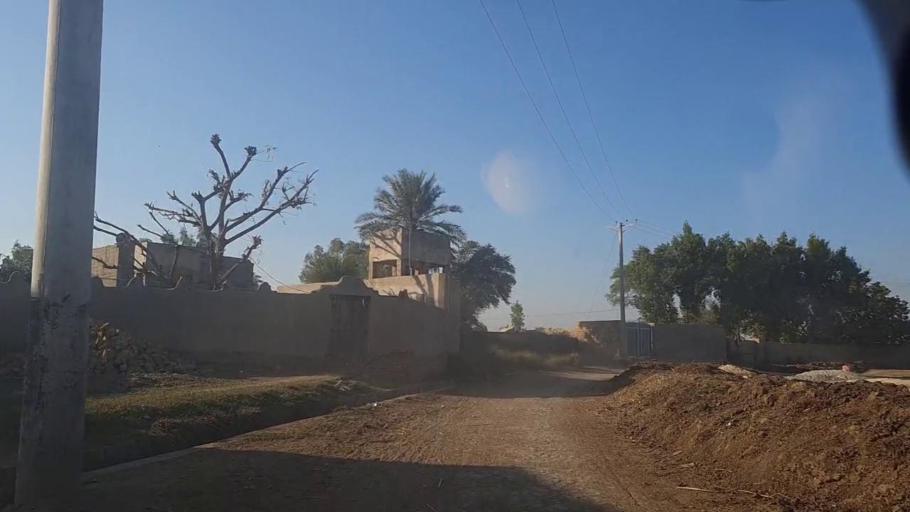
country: PK
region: Sindh
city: Sobhadero
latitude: 27.4005
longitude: 68.4212
